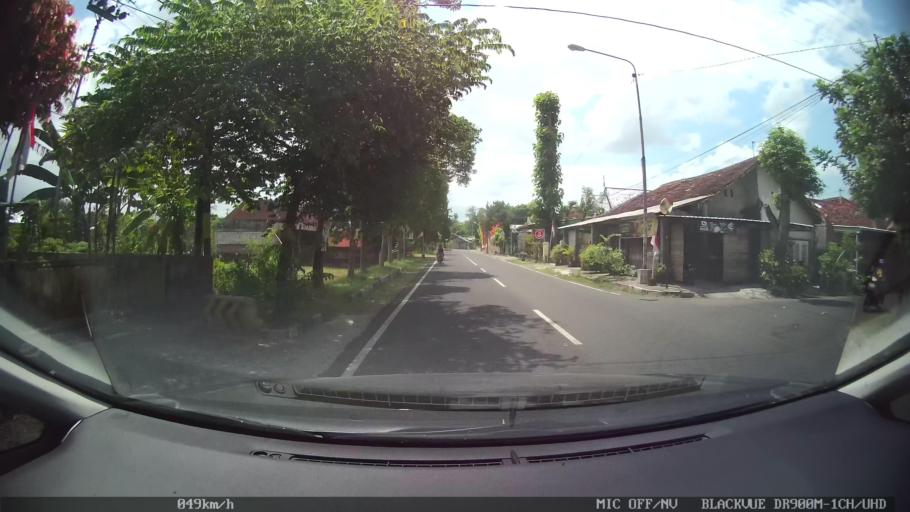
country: ID
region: Daerah Istimewa Yogyakarta
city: Bantul
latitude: -7.8815
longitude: 110.3360
